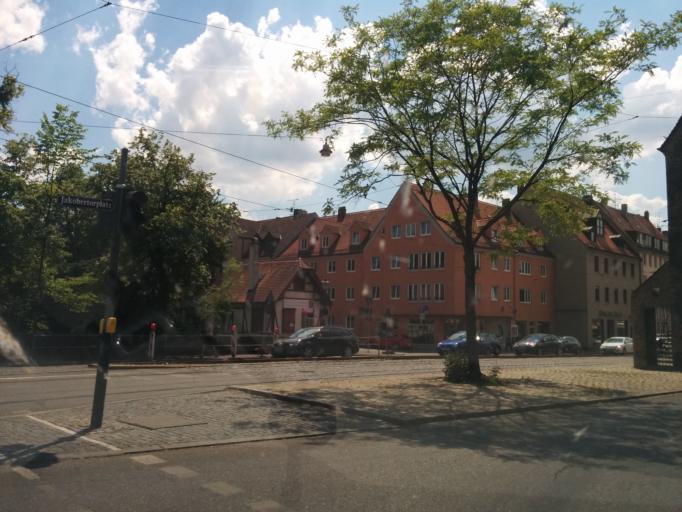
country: DE
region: Bavaria
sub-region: Swabia
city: Augsburg
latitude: 48.3705
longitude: 10.9092
